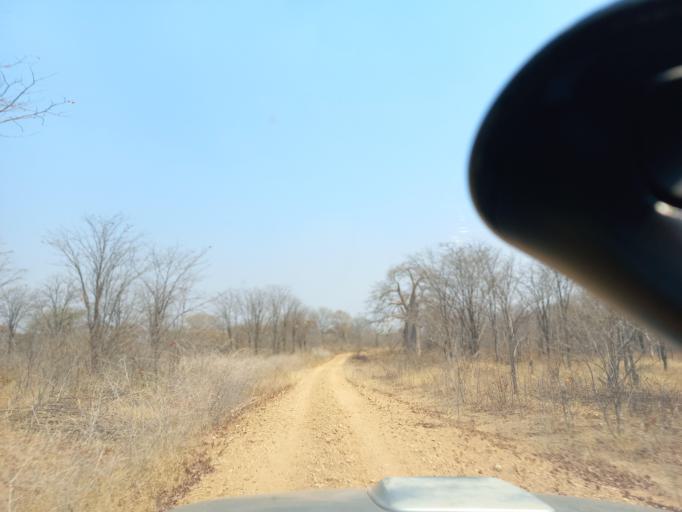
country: ZW
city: Chirundu
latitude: -15.8912
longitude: 28.7084
